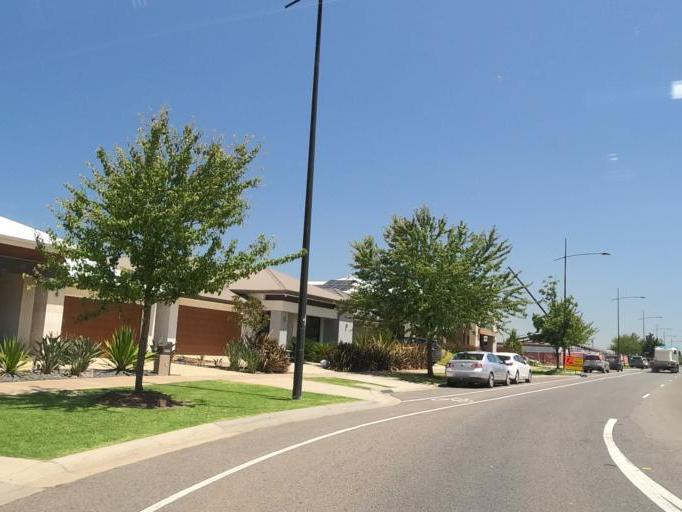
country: AU
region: Victoria
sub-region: Hume
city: Greenvale
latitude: -37.6227
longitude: 144.8823
